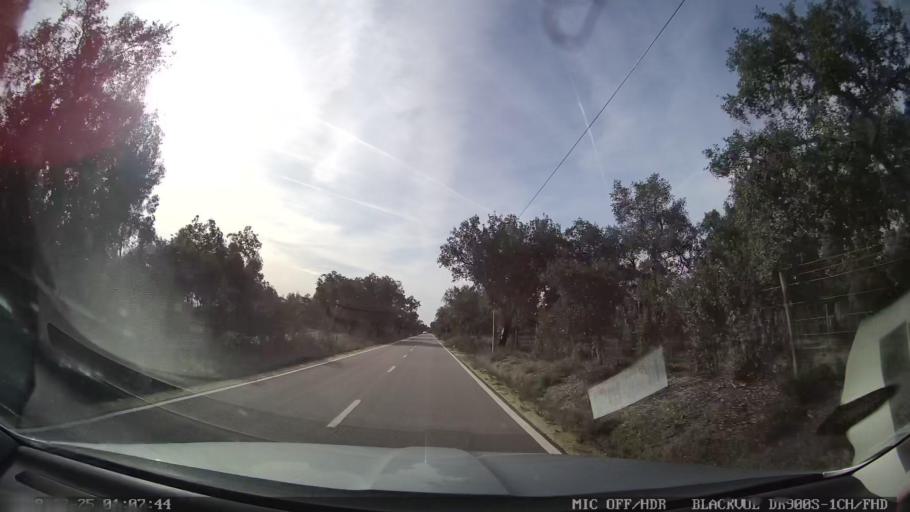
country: PT
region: Portalegre
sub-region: Nisa
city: Nisa
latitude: 39.4587
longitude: -7.7052
